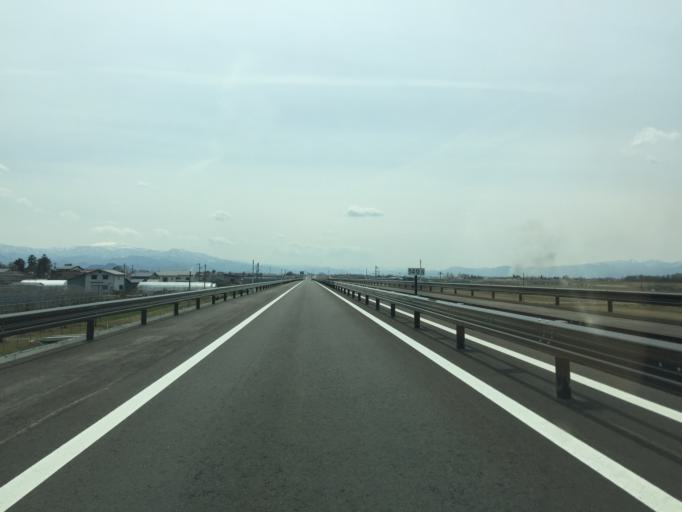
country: JP
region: Yamagata
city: Higashine
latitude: 38.4342
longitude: 140.3534
